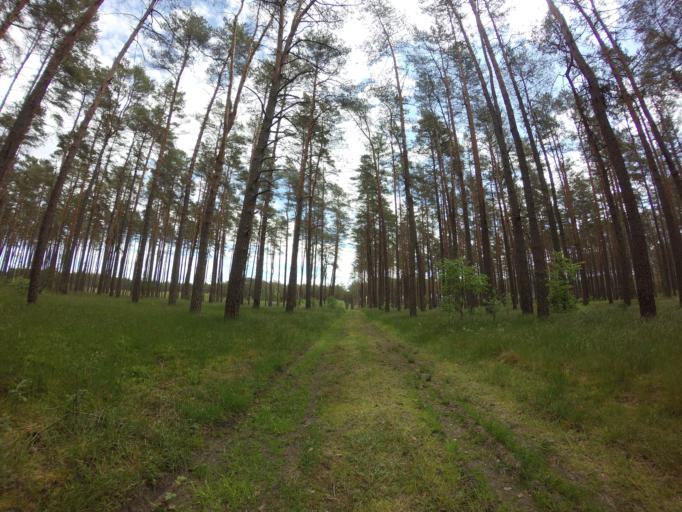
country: PL
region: West Pomeranian Voivodeship
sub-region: Powiat drawski
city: Kalisz Pomorski
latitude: 53.1601
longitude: 15.9714
